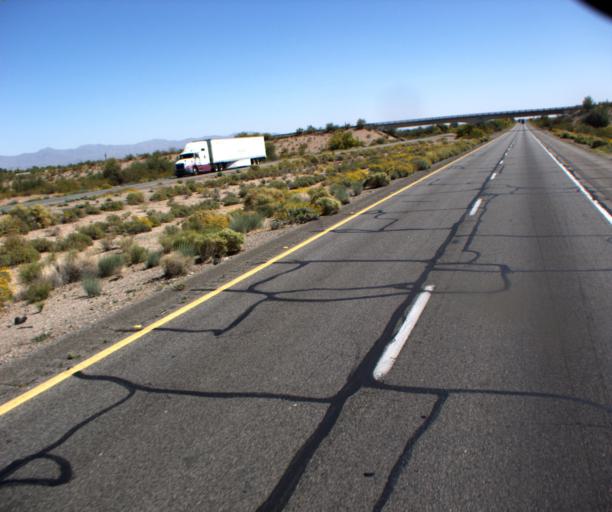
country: US
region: Arizona
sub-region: Maricopa County
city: Buckeye
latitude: 33.4707
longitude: -112.8184
